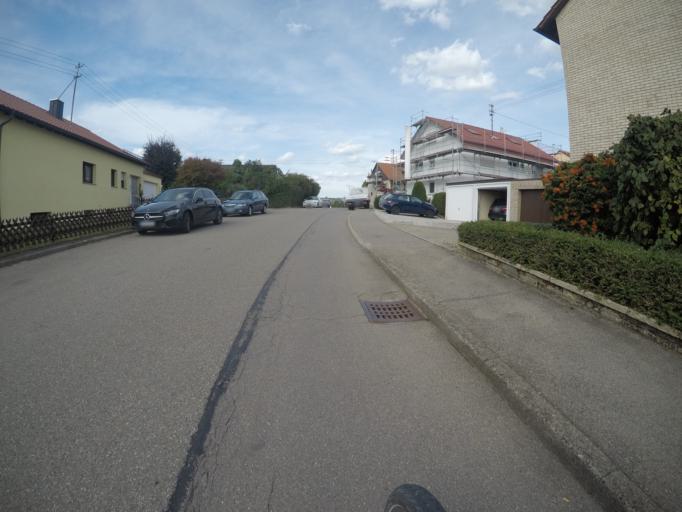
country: DE
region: Baden-Wuerttemberg
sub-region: Regierungsbezirk Stuttgart
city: Gartringen
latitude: 48.6415
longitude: 8.8892
